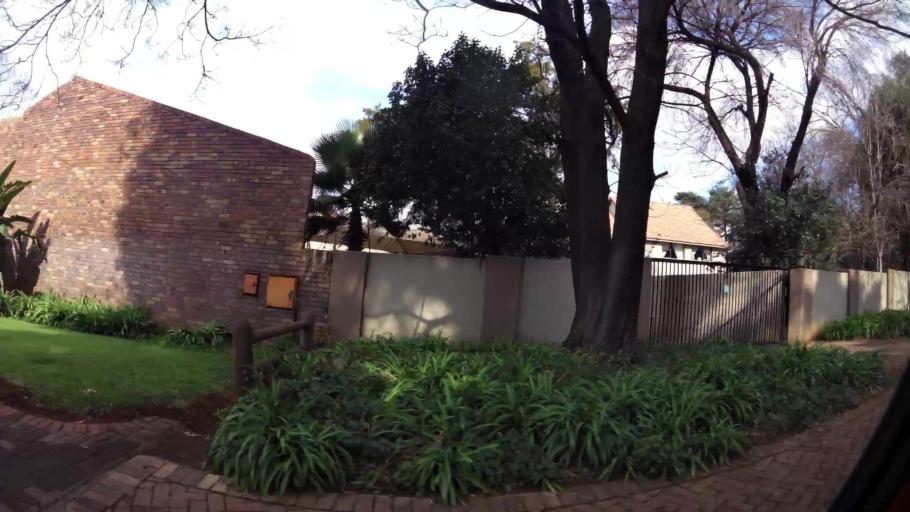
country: ZA
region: Gauteng
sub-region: Sedibeng District Municipality
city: Vanderbijlpark
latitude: -26.7358
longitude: 27.8362
